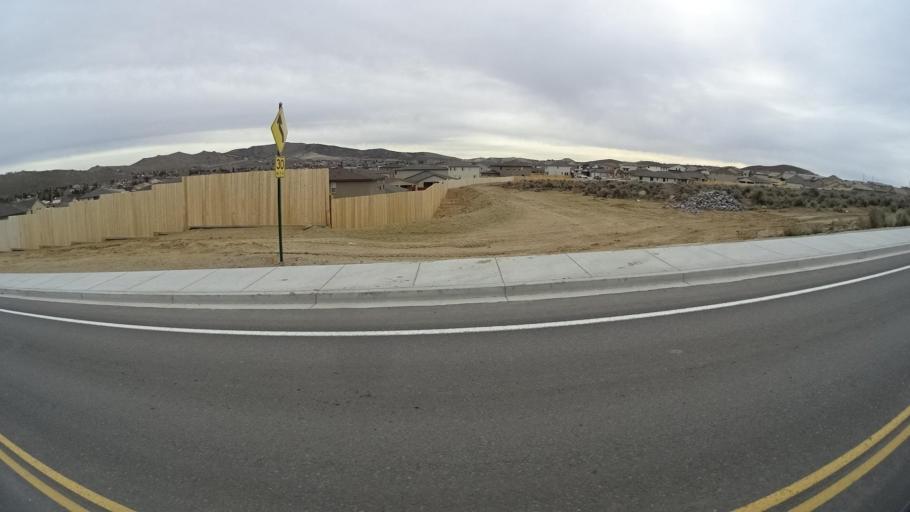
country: US
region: Nevada
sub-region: Washoe County
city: Golden Valley
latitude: 39.6114
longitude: -119.8449
